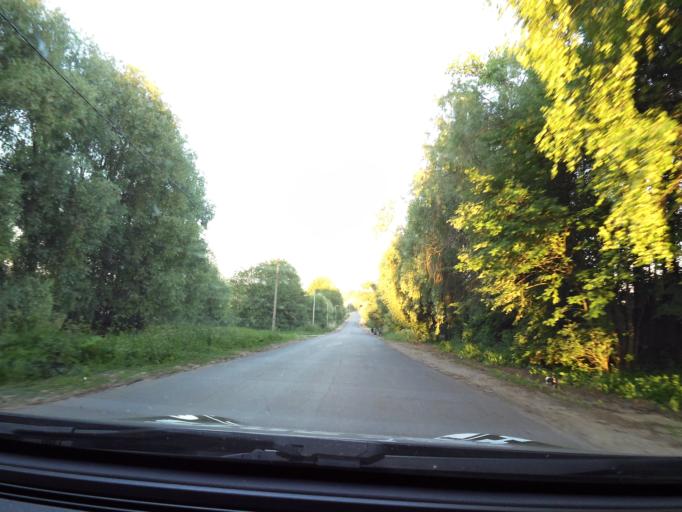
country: RU
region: Jaroslavl
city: Prechistoye
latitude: 58.4194
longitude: 40.3421
